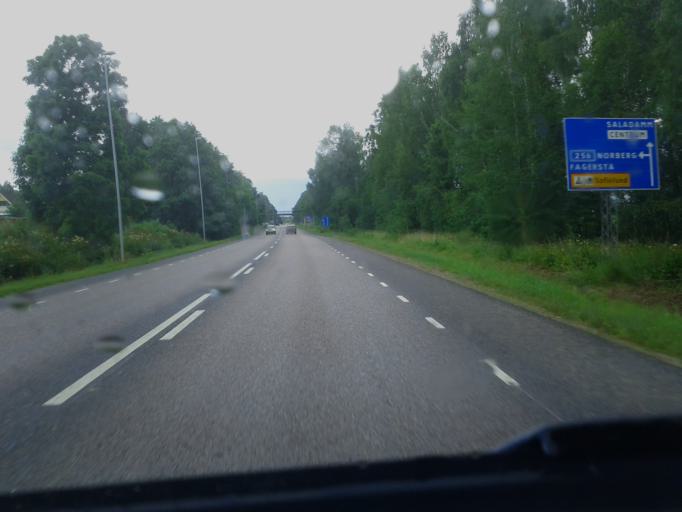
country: SE
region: Vaestmanland
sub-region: Sala Kommun
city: Sala
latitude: 59.9117
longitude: 16.5869
